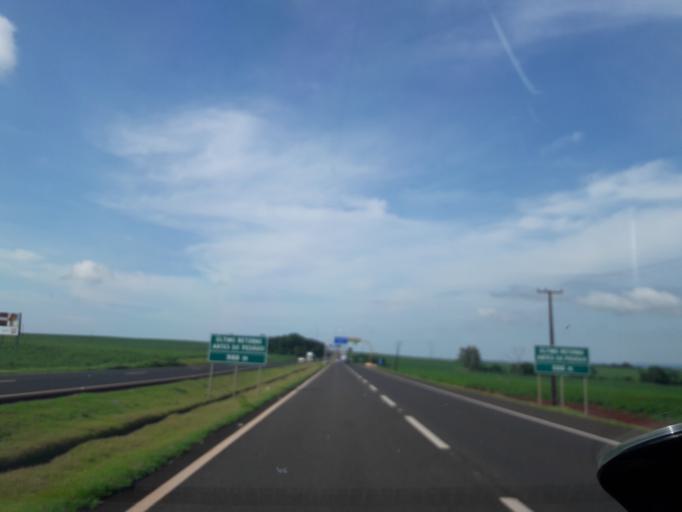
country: BR
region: Parana
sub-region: Paicandu
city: Paicandu
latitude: -23.6276
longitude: -52.1004
